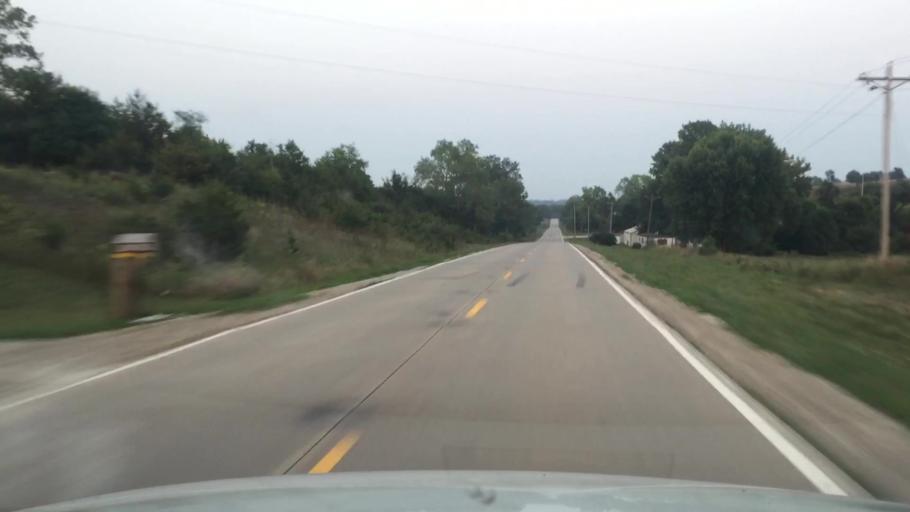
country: US
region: Iowa
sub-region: Warren County
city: Indianola
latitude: 41.1909
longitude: -93.6490
